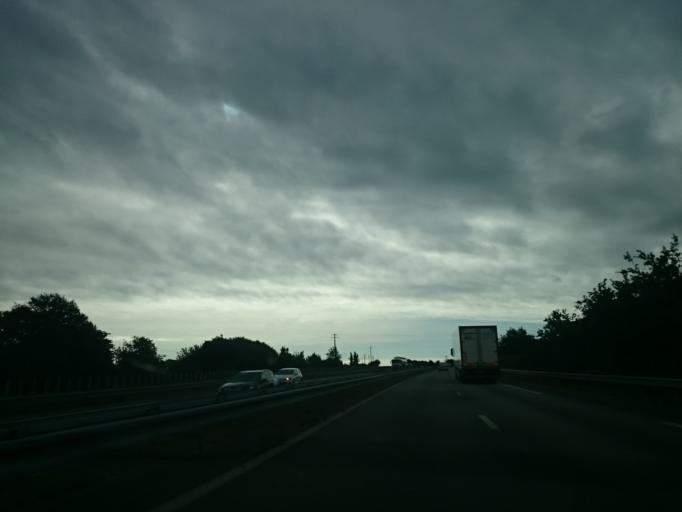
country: FR
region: Brittany
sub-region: Departement du Morbihan
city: Theix
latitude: 47.6245
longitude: -2.6322
